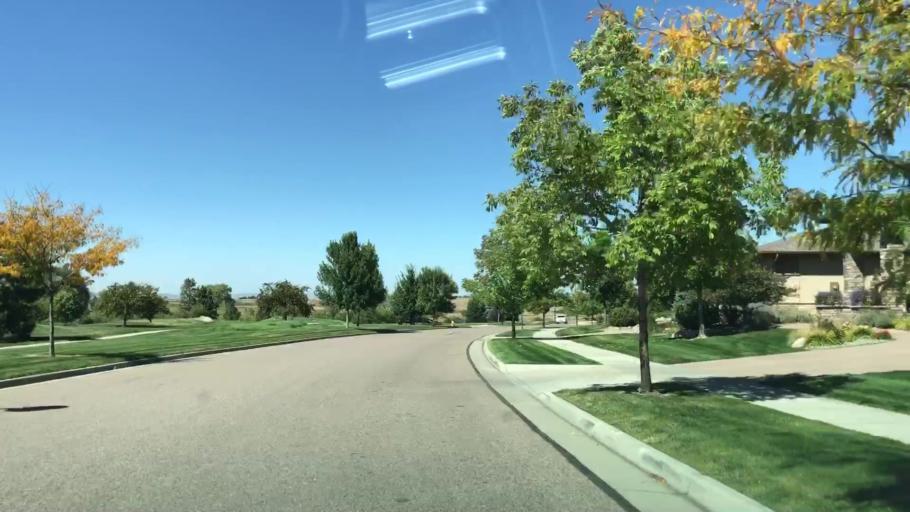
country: US
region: Colorado
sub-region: Weld County
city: Windsor
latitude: 40.5355
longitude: -104.9579
